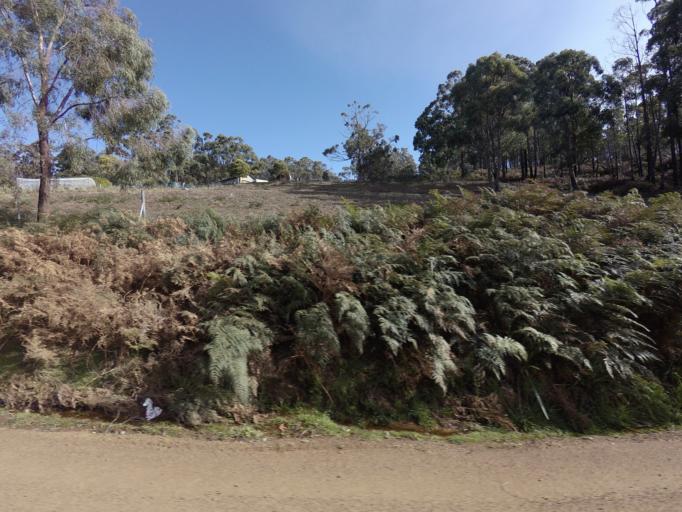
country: AU
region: Tasmania
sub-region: Kingborough
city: Kettering
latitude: -43.0856
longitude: 147.2638
